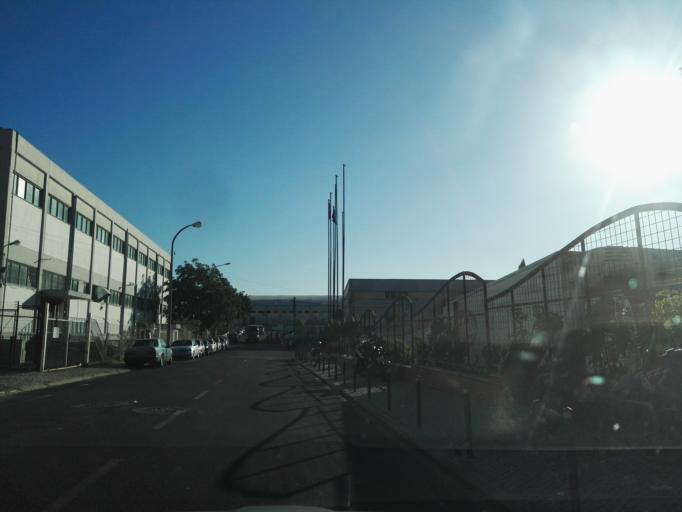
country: PT
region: Lisbon
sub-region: Loures
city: Camarate
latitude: 38.7876
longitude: -9.1252
